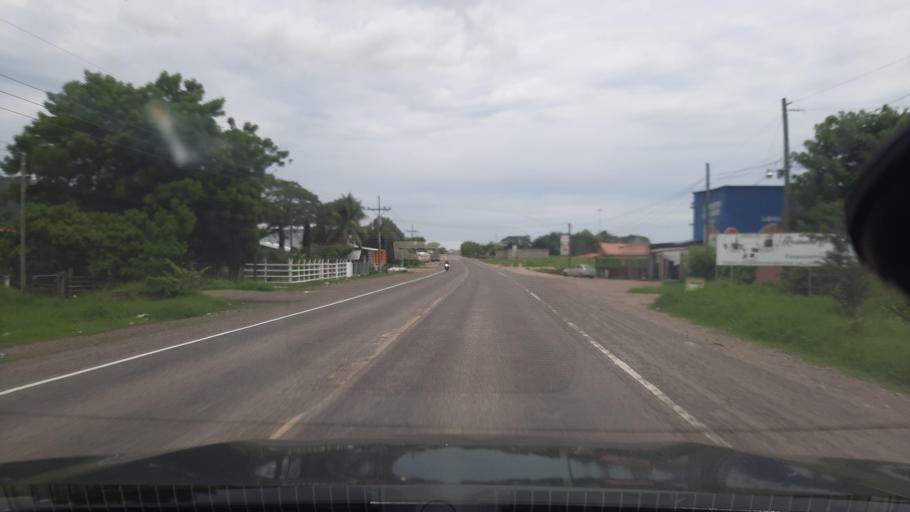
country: HN
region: Valle
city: Jicaro Galan
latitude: 13.4982
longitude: -87.4426
